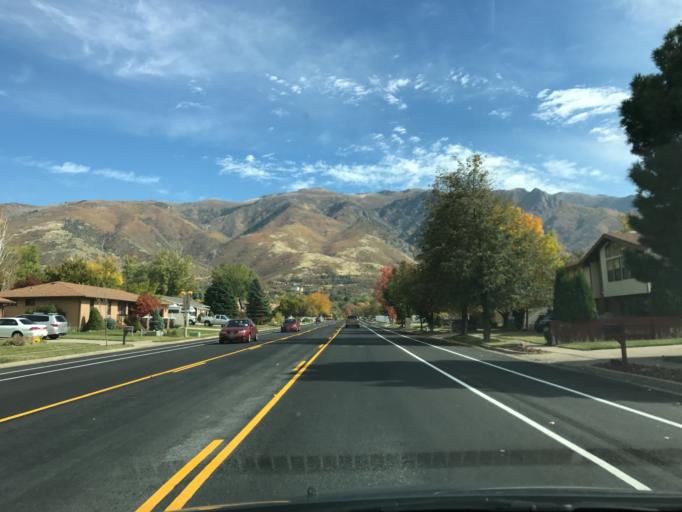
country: US
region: Utah
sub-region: Davis County
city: South Weber
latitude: 41.0891
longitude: -111.9252
